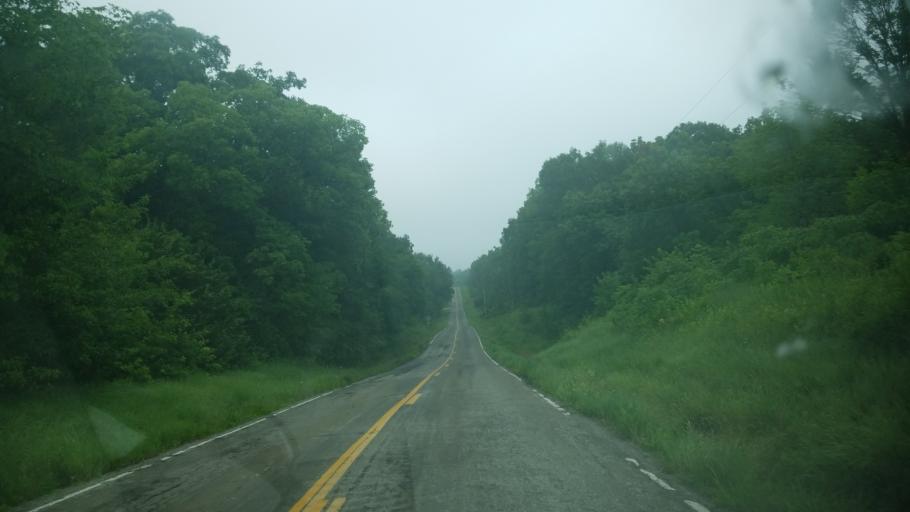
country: US
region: Missouri
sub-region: Audrain County
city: Vandalia
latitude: 39.2890
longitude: -91.3508
